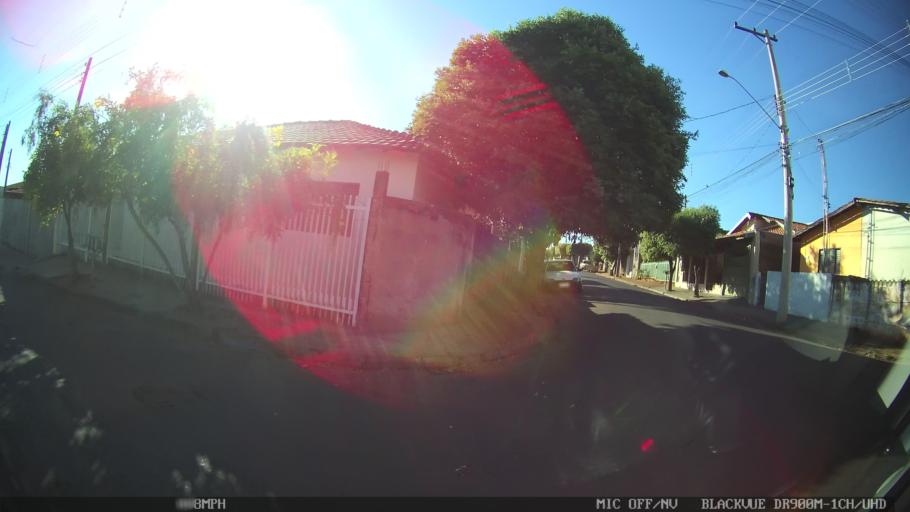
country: BR
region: Sao Paulo
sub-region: Olimpia
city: Olimpia
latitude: -20.7281
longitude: -48.9074
